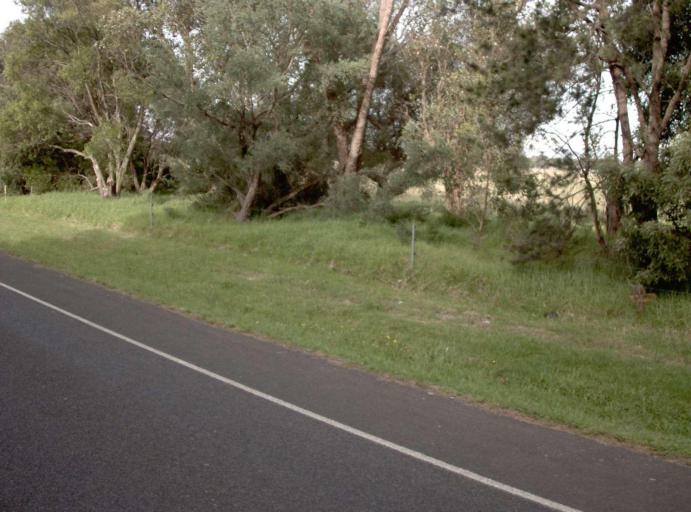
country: AU
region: Victoria
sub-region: Latrobe
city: Traralgon
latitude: -38.1383
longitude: 146.5571
